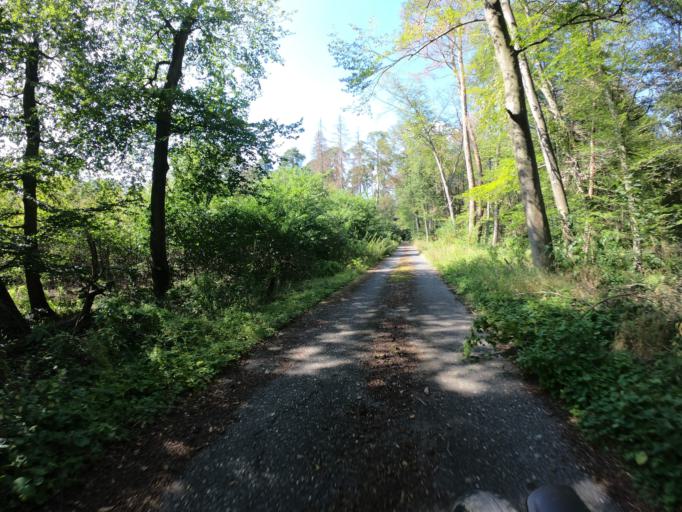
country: DE
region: Hesse
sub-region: Regierungsbezirk Darmstadt
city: Erzhausen
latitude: 49.9880
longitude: 8.6291
